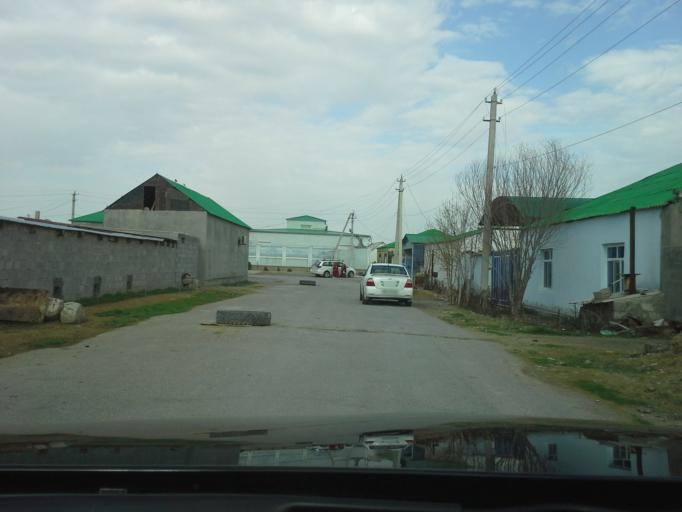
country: TM
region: Ahal
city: Ashgabat
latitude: 37.9896
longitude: 58.2905
